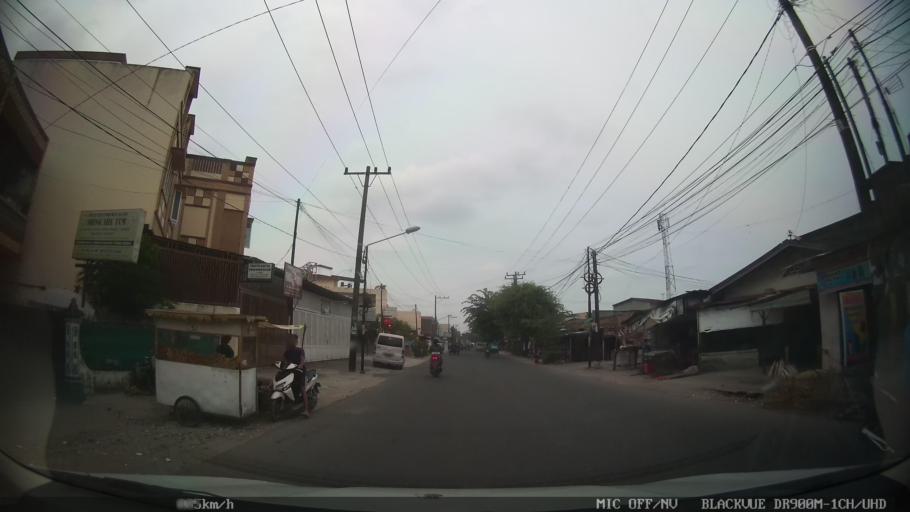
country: ID
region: North Sumatra
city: Medan
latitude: 3.5747
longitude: 98.7260
